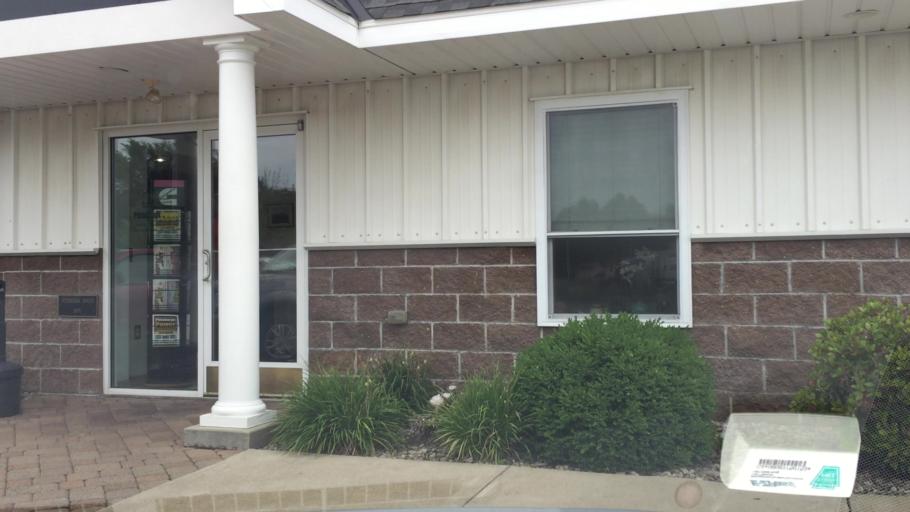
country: US
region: Pennsylvania
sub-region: Butler County
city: Saxonburg
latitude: 40.7333
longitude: -79.8443
